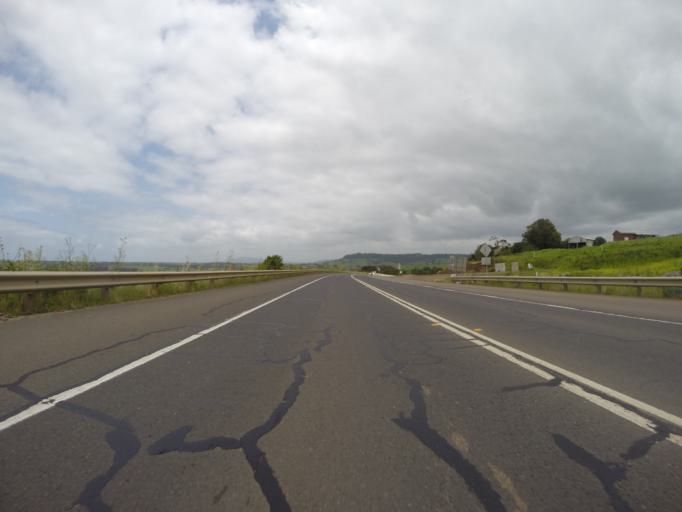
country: AU
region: New South Wales
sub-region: Kiama
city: Gerringong
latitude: -34.7478
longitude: 150.8007
